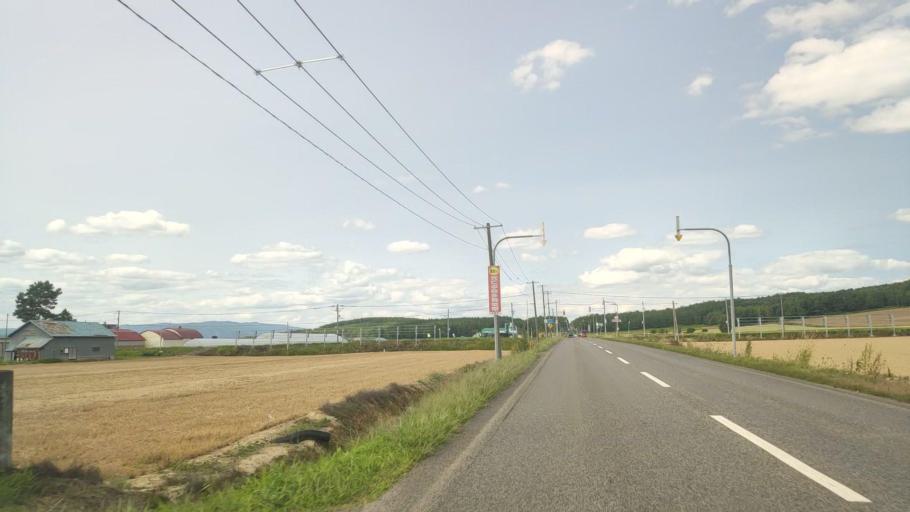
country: JP
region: Hokkaido
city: Nayoro
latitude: 44.2347
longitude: 142.4157
